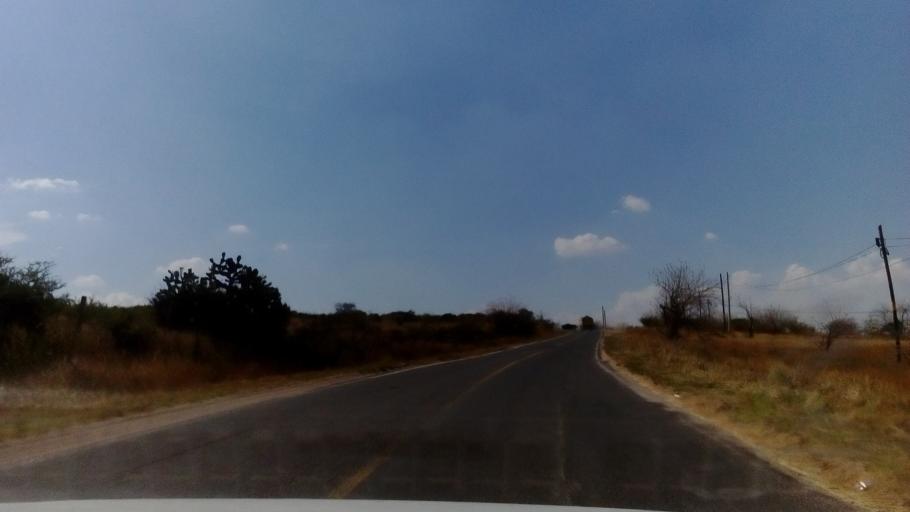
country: MX
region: Guanajuato
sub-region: Silao de la Victoria
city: San Francisco (Banos de Agua Caliente)
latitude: 21.0742
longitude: -101.4876
